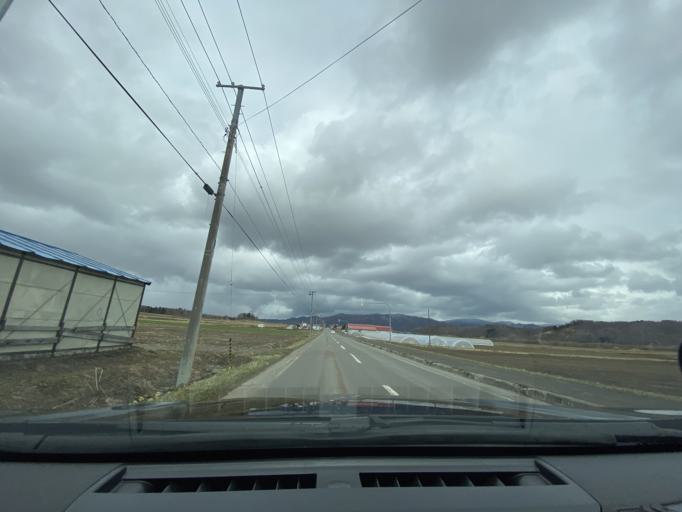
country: JP
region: Hokkaido
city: Nayoro
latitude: 44.0962
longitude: 142.4742
